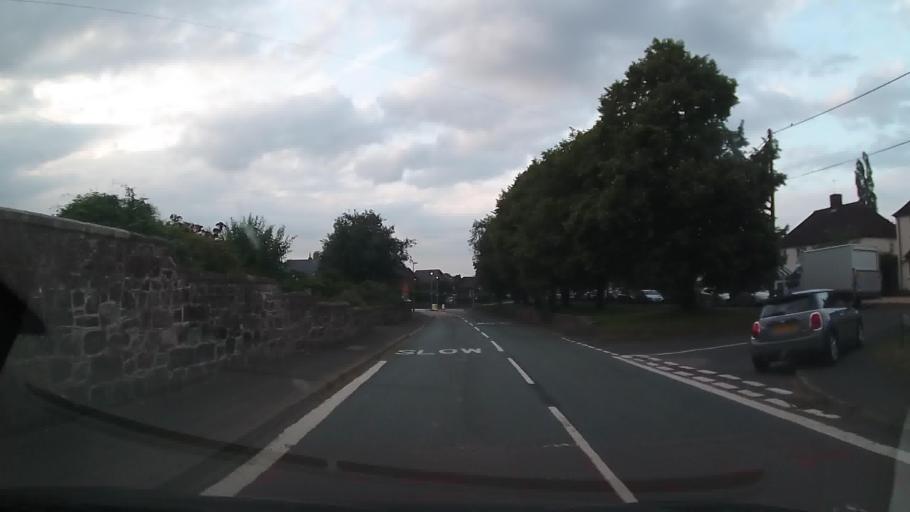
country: GB
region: England
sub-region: Shropshire
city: Petton
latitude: 52.8084
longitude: -2.7907
